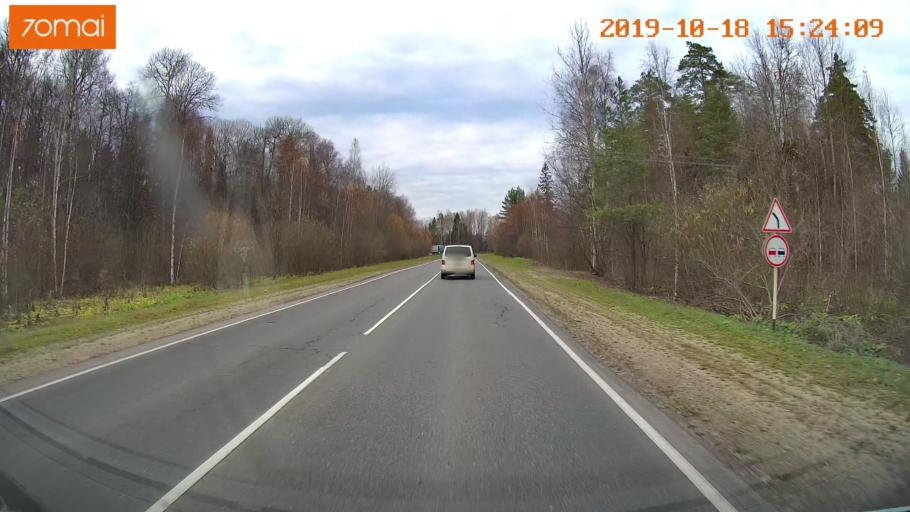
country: RU
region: Vladimir
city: Anopino
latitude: 55.7309
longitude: 40.7250
